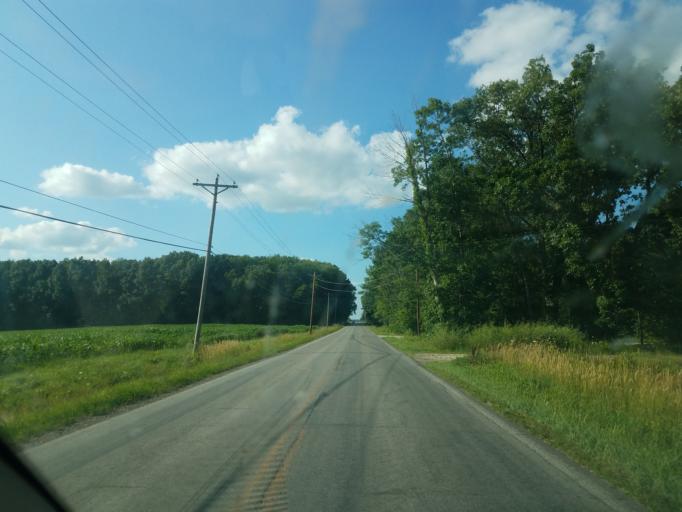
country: US
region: Ohio
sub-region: Wayne County
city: Apple Creek
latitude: 40.7384
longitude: -81.8961
